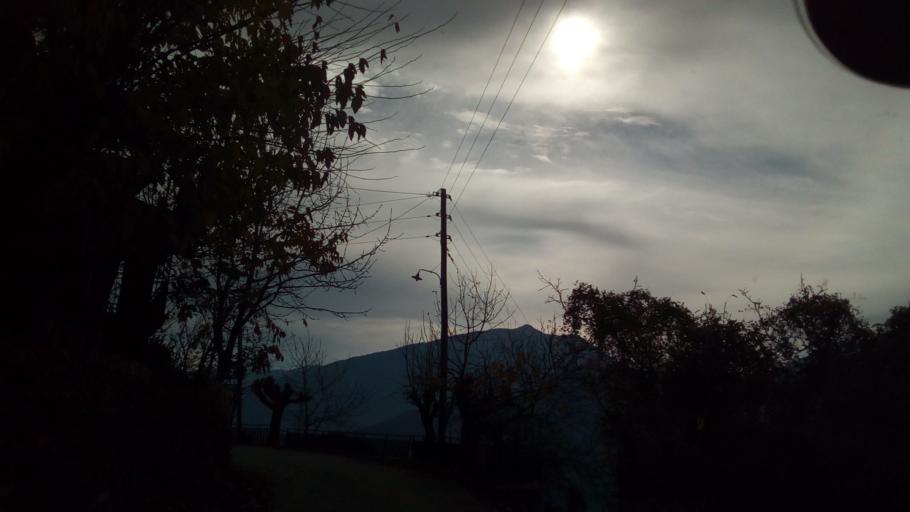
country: GR
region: West Greece
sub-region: Nomos Aitolias kai Akarnanias
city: Thermo
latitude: 38.6859
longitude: 21.8634
